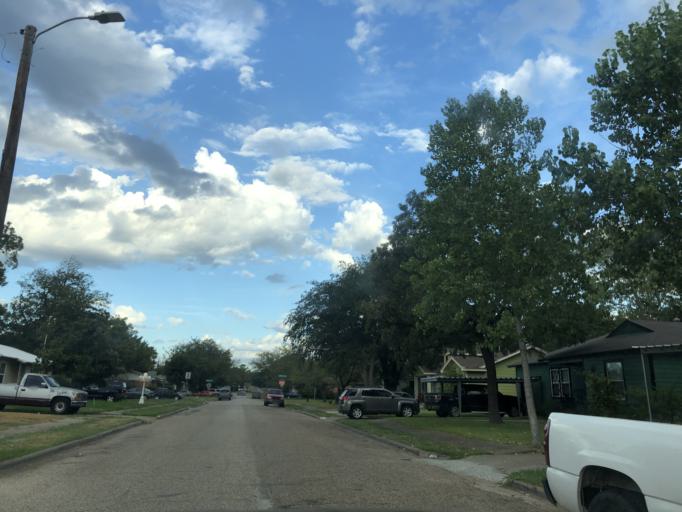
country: US
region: Texas
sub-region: Dallas County
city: Garland
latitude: 32.8745
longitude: -96.6514
